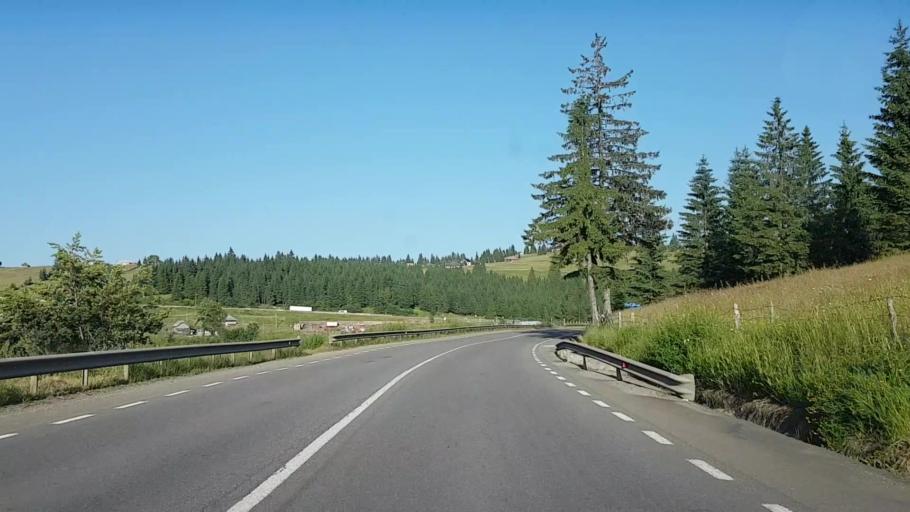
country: RO
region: Bistrita-Nasaud
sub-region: Comuna Lunca Ilvei
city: Lunca Ilvei
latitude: 47.2419
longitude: 25.0119
